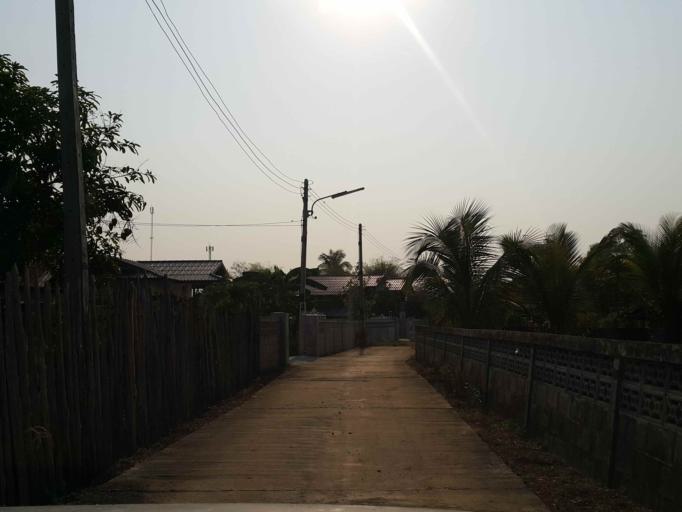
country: TH
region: Sukhothai
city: Thung Saliam
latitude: 17.3249
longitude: 99.4504
